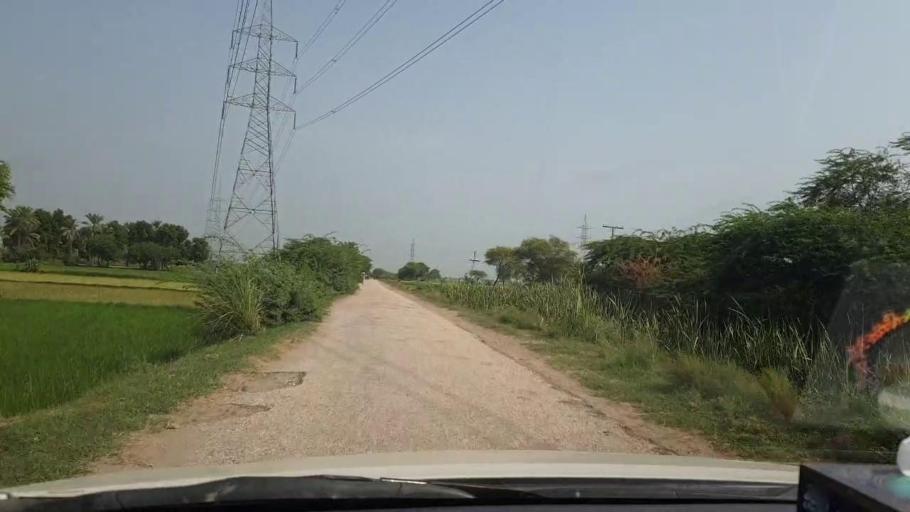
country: PK
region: Sindh
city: Shikarpur
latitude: 27.9783
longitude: 68.6642
